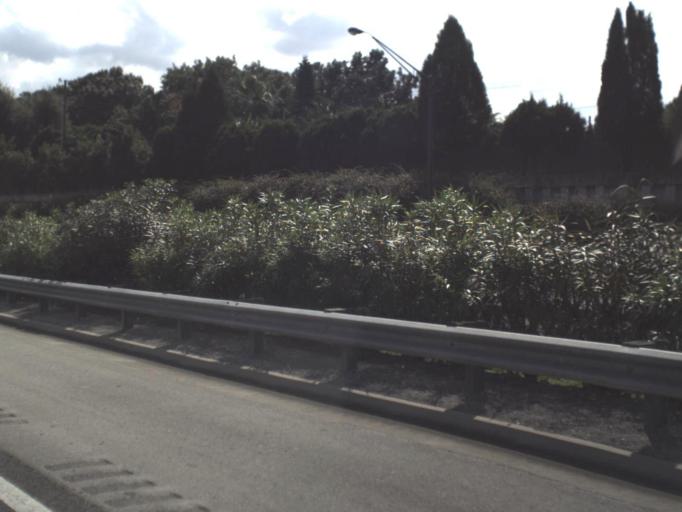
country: US
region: Florida
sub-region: Polk County
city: Medulla
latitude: 27.9954
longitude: -81.9548
